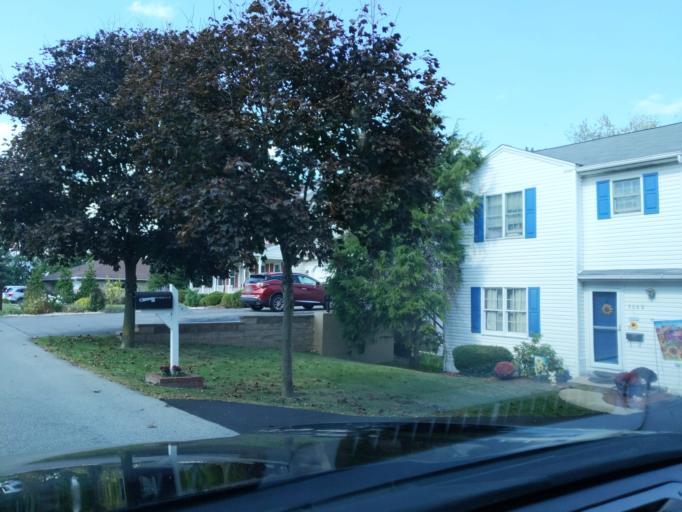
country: US
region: Pennsylvania
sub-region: Blair County
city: Altoona
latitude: 40.4981
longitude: -78.4001
